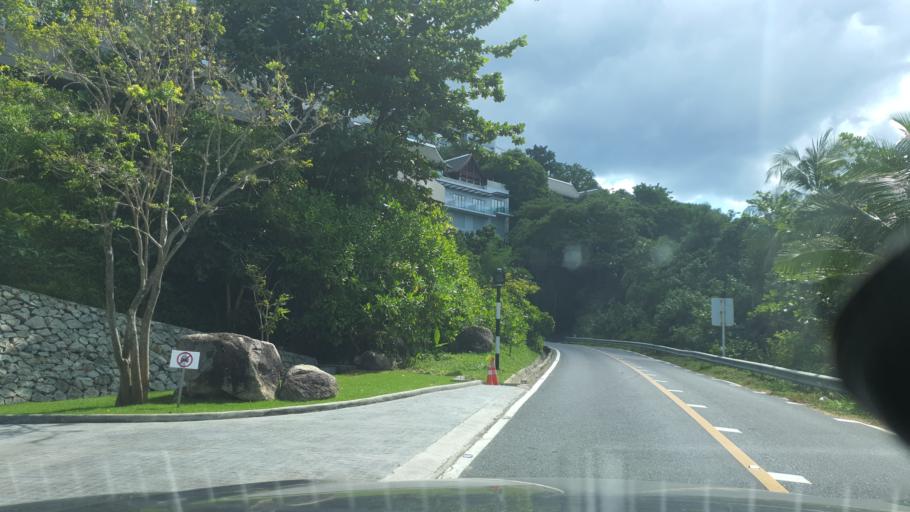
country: TH
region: Phuket
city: Thalang
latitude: 8.0545
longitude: 98.2785
